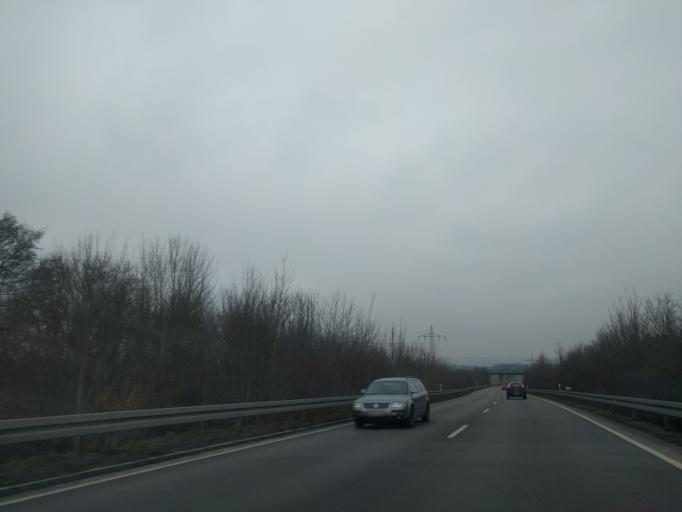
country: DE
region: Bavaria
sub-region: Swabia
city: Genderkingen
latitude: 48.6982
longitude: 10.8884
